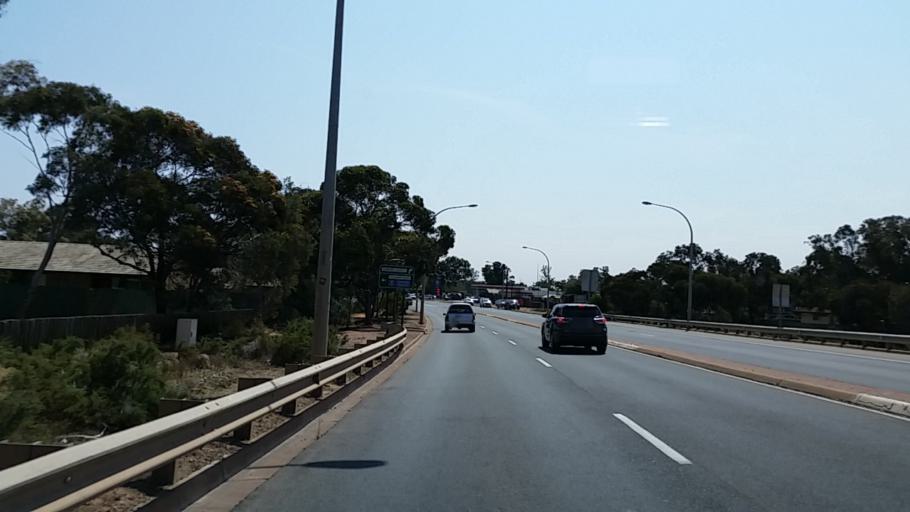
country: AU
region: South Australia
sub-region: Port Augusta
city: Port Augusta
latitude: -32.5018
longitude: 137.7801
